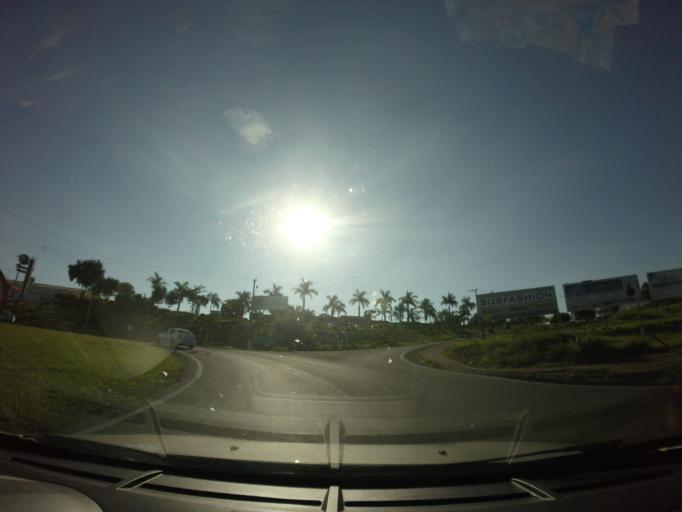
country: BR
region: Sao Paulo
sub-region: Rio Claro
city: Rio Claro
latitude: -22.4199
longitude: -47.5786
